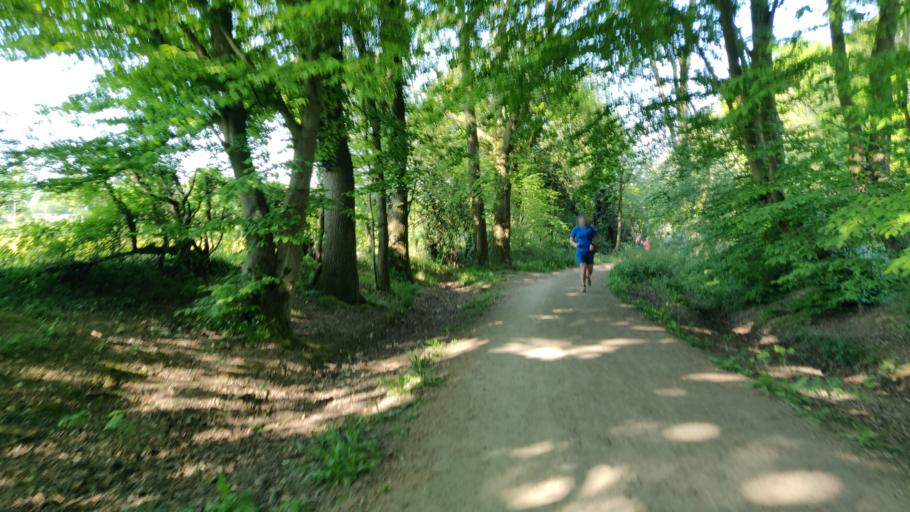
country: GB
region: England
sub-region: West Sussex
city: Southwater
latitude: 51.0594
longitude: -0.3729
